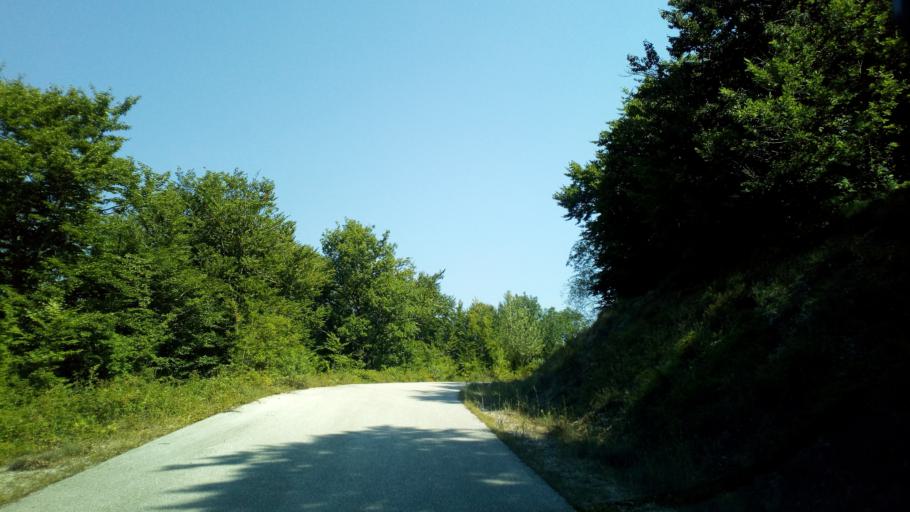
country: GR
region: Central Macedonia
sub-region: Nomos Thessalonikis
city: Sochos
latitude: 40.8279
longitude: 23.3509
